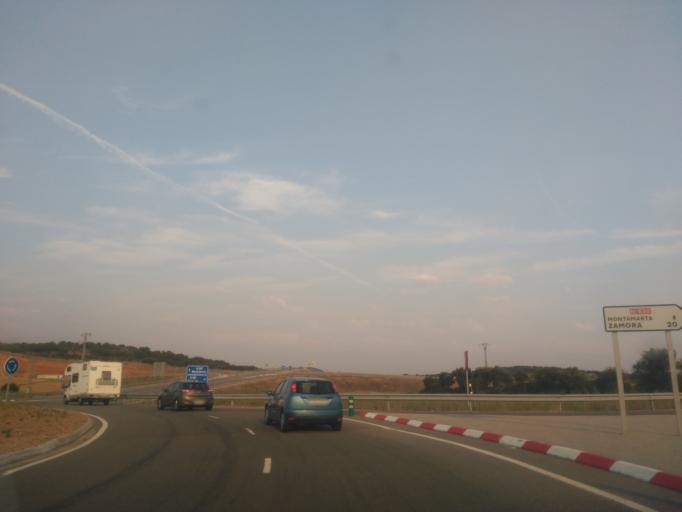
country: ES
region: Castille and Leon
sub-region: Provincia de Zamora
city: Montamarta
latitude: 41.6889
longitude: -5.8078
